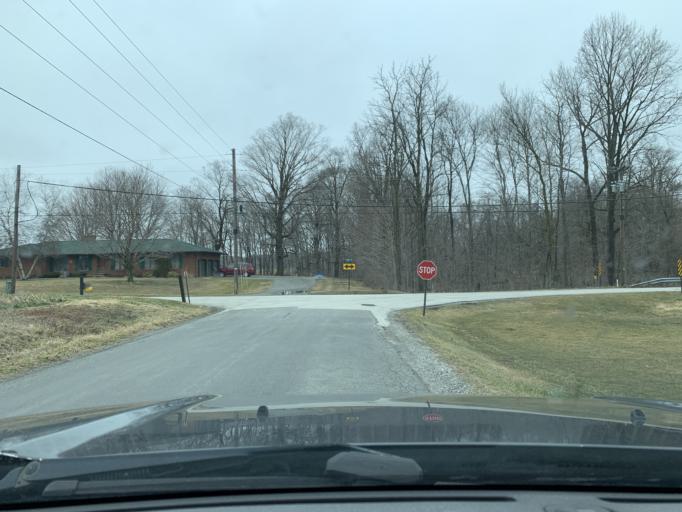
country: US
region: Indiana
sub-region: Porter County
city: Chesterton
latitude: 41.6067
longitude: -86.9901
